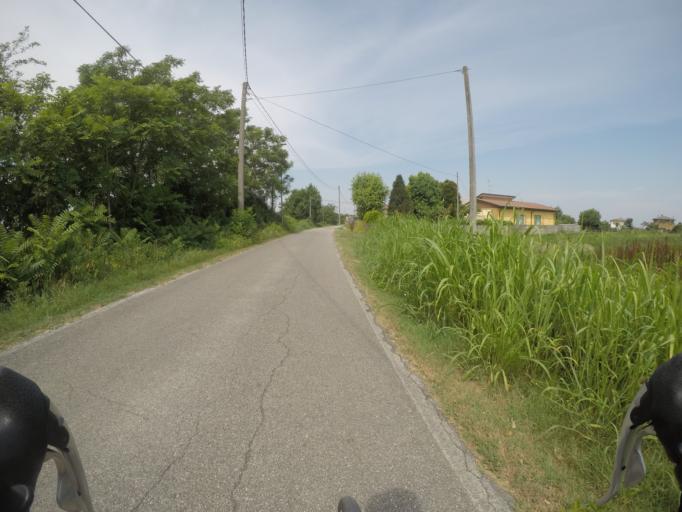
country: IT
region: Veneto
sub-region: Provincia di Rovigo
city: Villanova del Ghebbo Canton
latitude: 45.0500
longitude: 11.6535
